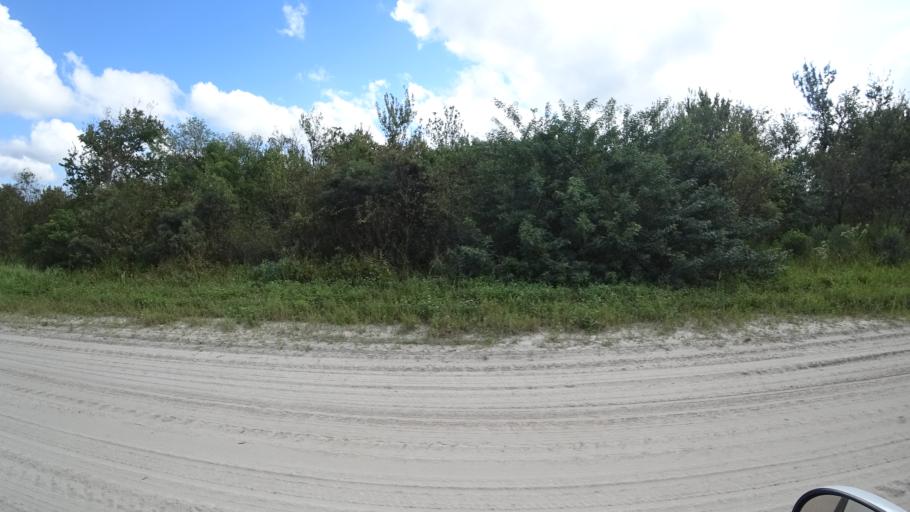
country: US
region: Florida
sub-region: Hillsborough County
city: Wimauma
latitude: 27.4425
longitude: -82.1826
